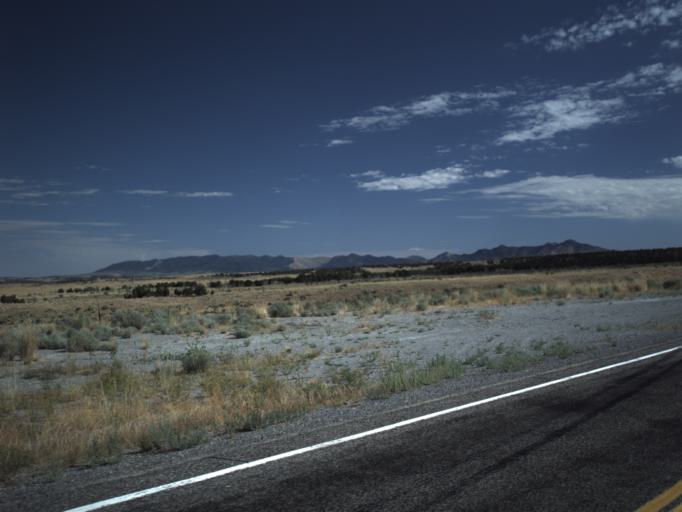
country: US
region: Utah
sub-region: Juab County
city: Mona
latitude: 39.7605
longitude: -112.1772
